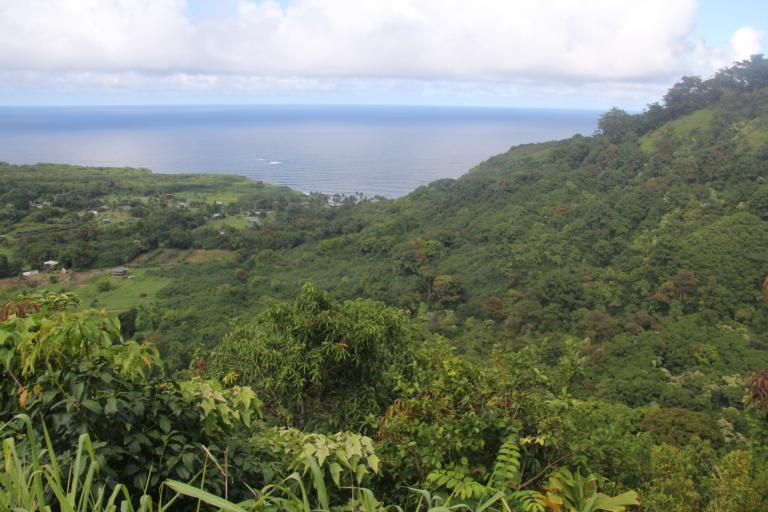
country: US
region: Hawaii
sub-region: Maui County
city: Wailua
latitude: 20.8369
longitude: -156.1380
